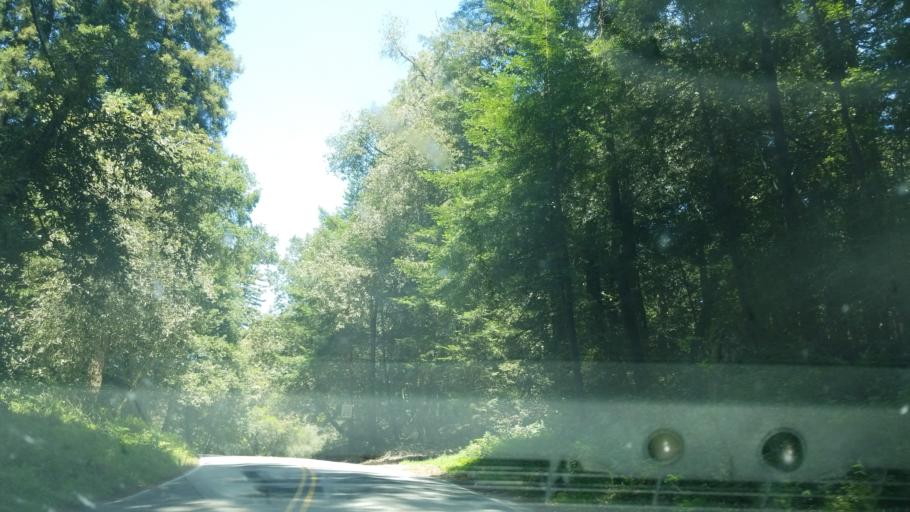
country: US
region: California
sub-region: Santa Cruz County
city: Interlaken
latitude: 37.0010
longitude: -121.7106
